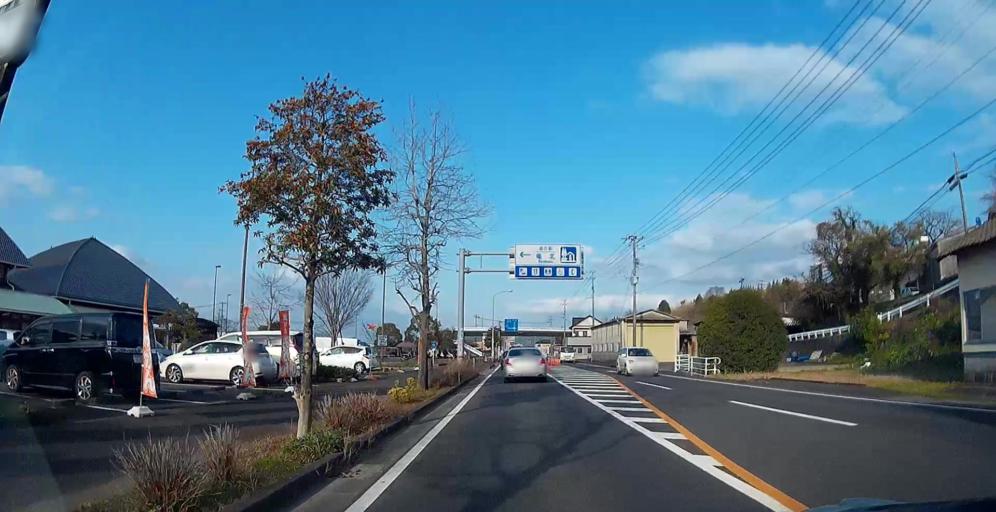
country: JP
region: Kumamoto
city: Matsubase
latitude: 32.5767
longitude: 130.6952
